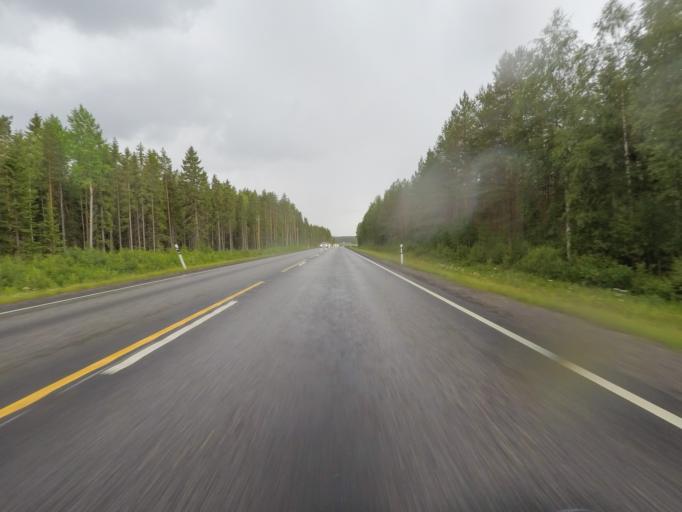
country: FI
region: Central Finland
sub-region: Jyvaeskylae
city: Hankasalmi
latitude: 62.3841
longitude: 26.6030
